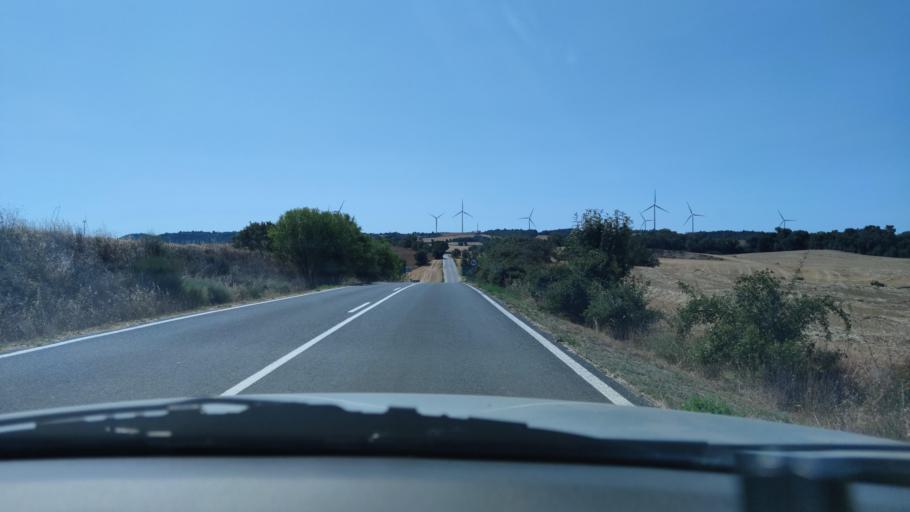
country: ES
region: Catalonia
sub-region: Provincia de Tarragona
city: Santa Coloma de Queralt
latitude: 41.5697
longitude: 1.3478
